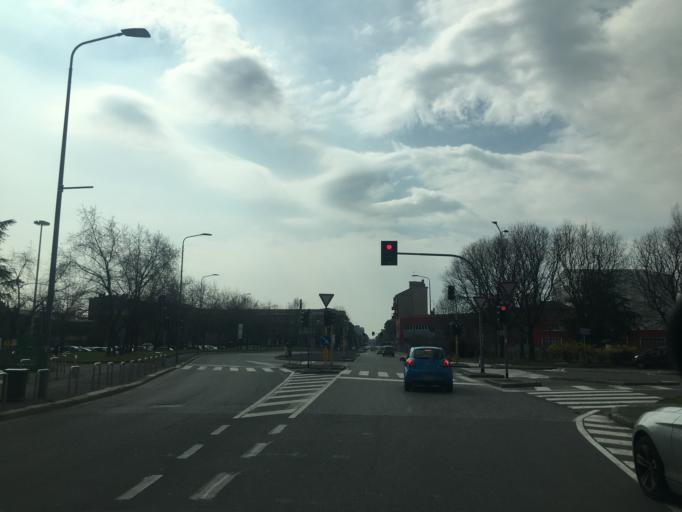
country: IT
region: Lombardy
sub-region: Citta metropolitana di Milano
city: Bresso
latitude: 45.5212
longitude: 9.2061
